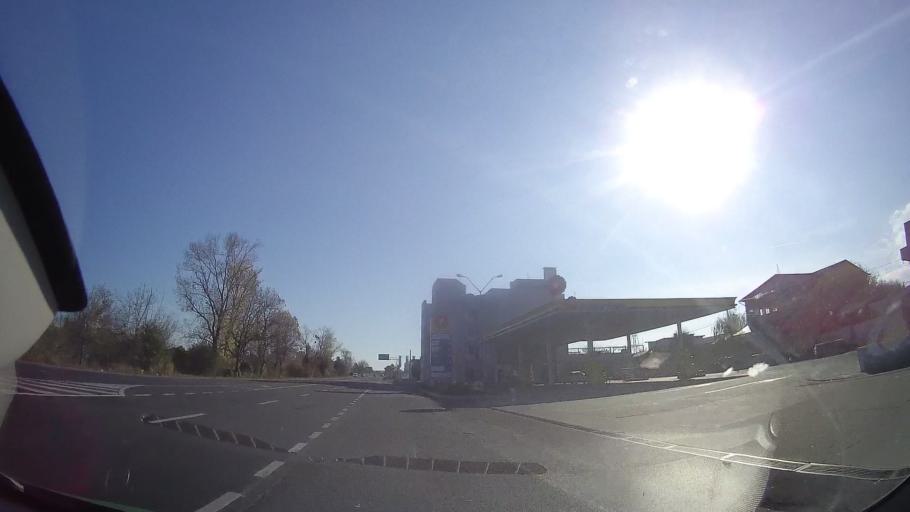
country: RO
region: Constanta
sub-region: Municipiul Mangalia
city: Mangalia
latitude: 43.8323
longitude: 28.5786
